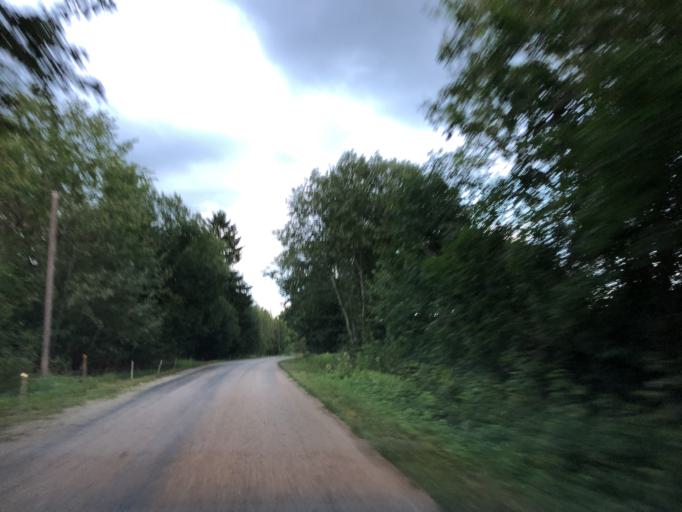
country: EE
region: Laeaene
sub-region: Ridala Parish
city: Uuemoisa
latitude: 58.8782
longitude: 23.6372
